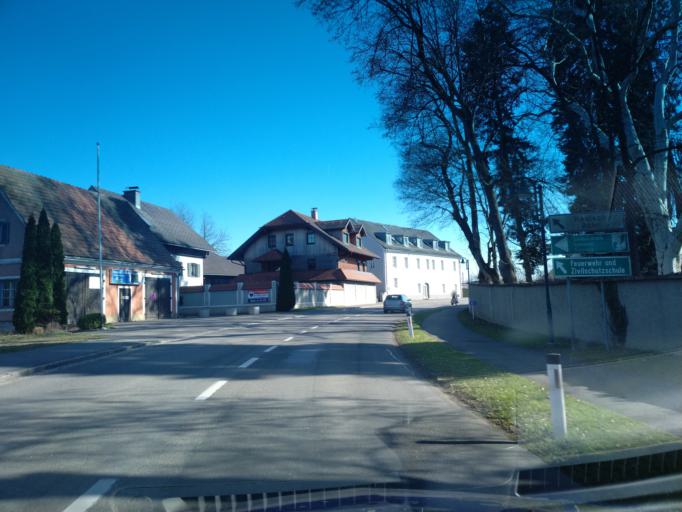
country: AT
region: Styria
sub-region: Politischer Bezirk Leibnitz
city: Stocking
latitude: 46.8555
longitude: 15.5377
